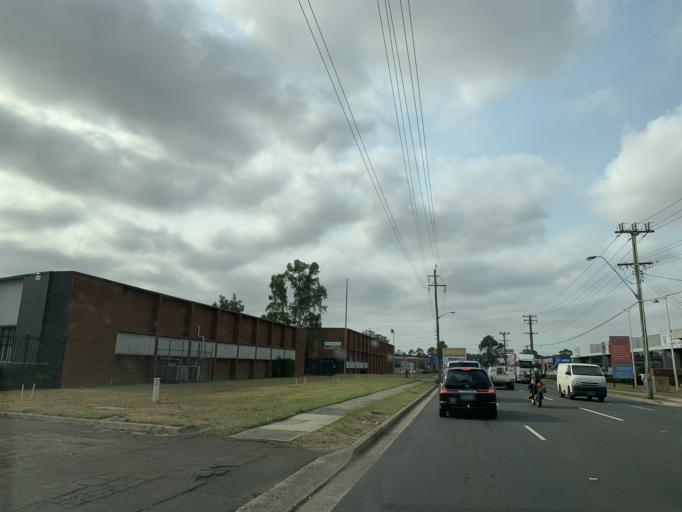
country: AU
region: New South Wales
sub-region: Holroyd
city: Girraween
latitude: -33.7722
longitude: 150.9440
